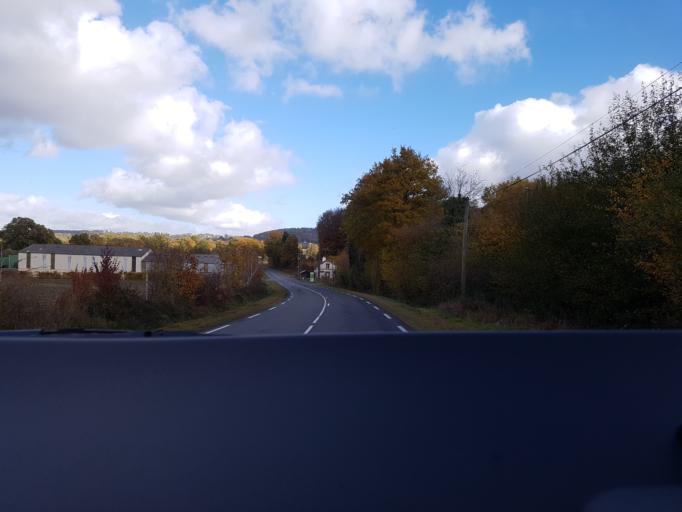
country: FR
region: Lower Normandy
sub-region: Departement de l'Orne
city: La Ferriere-aux-Etangs
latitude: 48.6430
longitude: -0.5425
